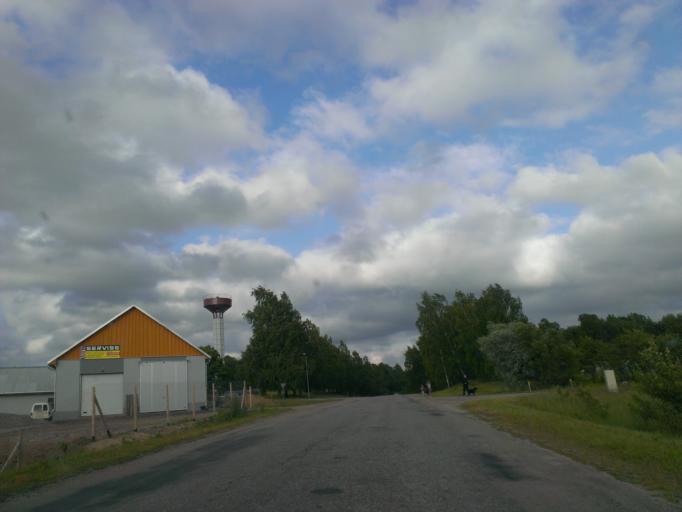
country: LV
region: Aizpute
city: Aizpute
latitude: 56.7308
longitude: 21.7248
